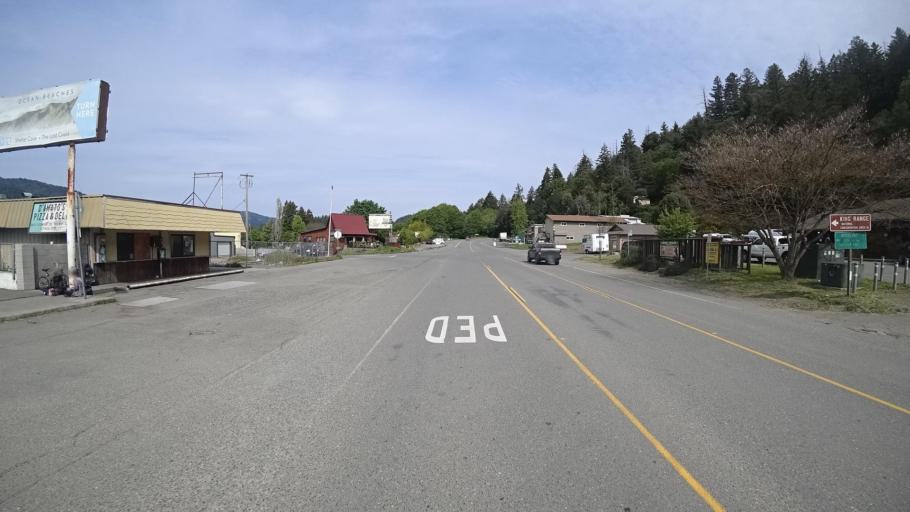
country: US
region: California
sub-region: Humboldt County
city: Redway
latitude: 40.1207
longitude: -123.8236
